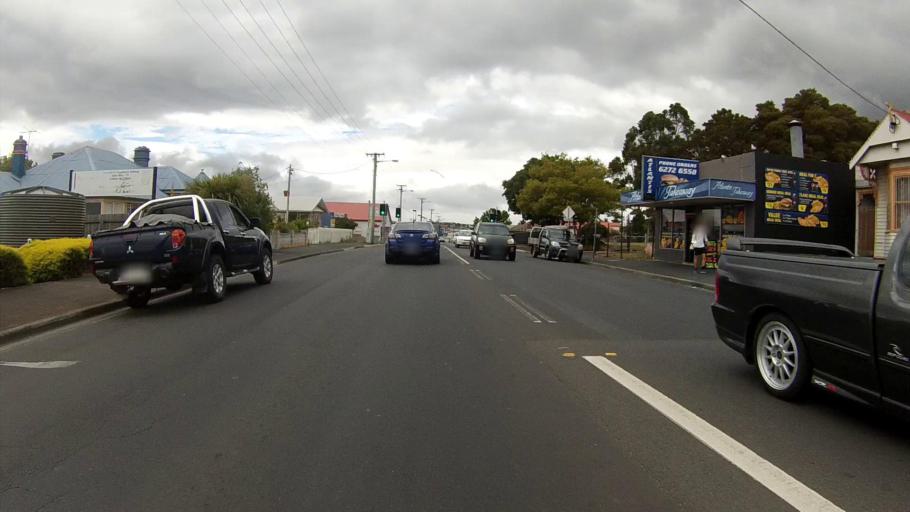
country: AU
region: Tasmania
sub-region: Glenorchy
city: Glenorchy
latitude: -42.8344
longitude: 147.2833
